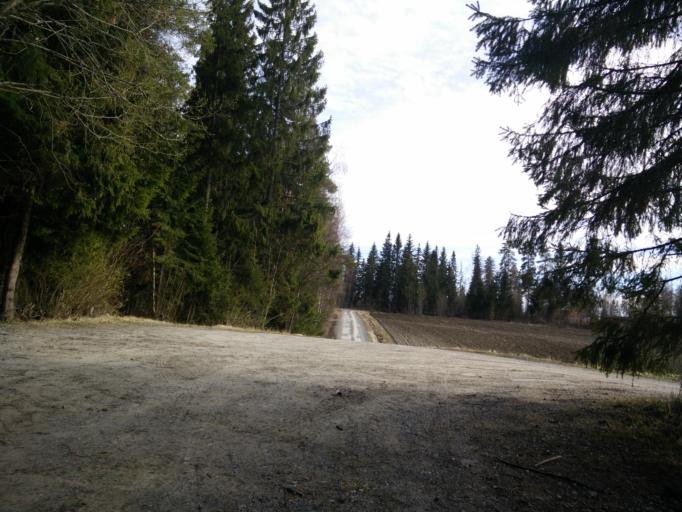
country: FI
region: Pirkanmaa
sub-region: Tampere
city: Orivesi
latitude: 61.6992
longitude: 24.3652
